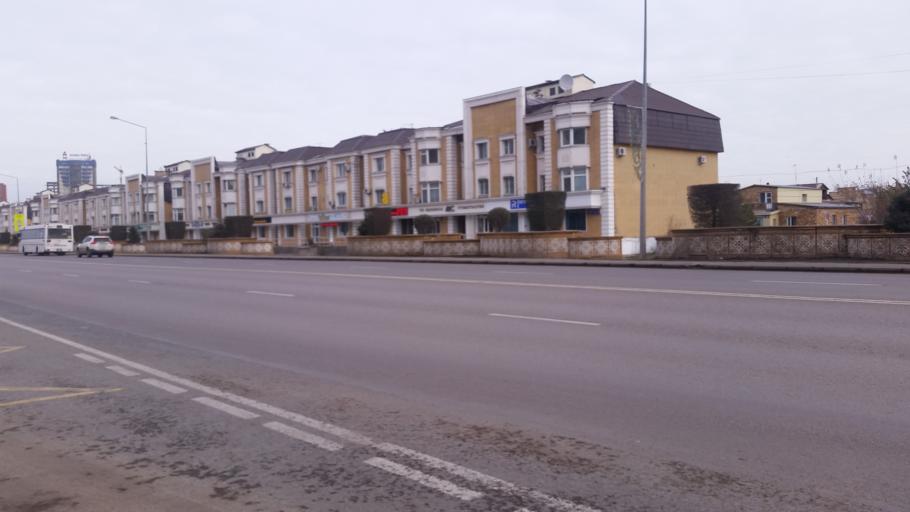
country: KZ
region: Astana Qalasy
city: Astana
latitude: 51.1405
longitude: 71.4181
